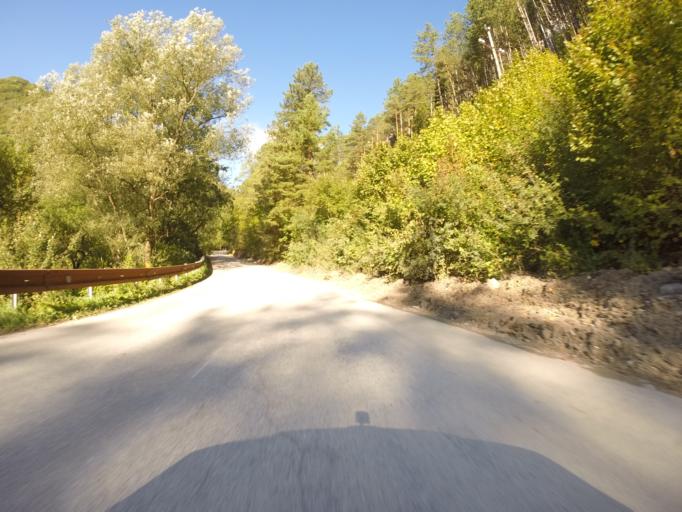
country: SK
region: Trenciansky
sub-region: Okres Povazska Bystrica
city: Povazska Bystrica
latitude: 48.9647
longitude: 18.4077
